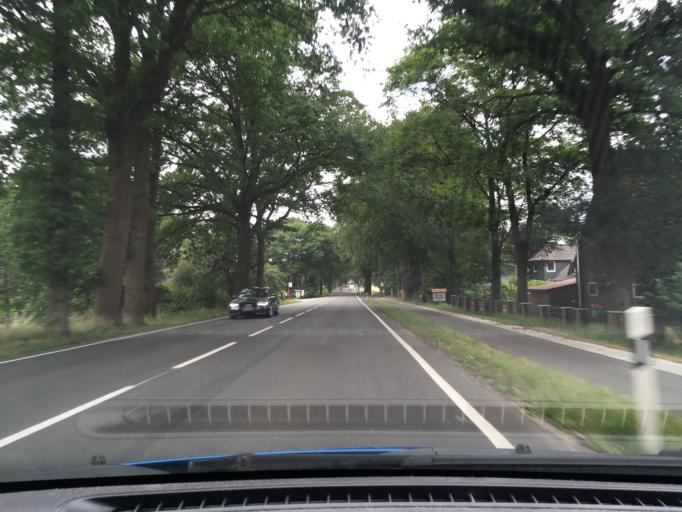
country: DE
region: Lower Saxony
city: Drestedt
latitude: 53.3317
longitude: 9.8129
